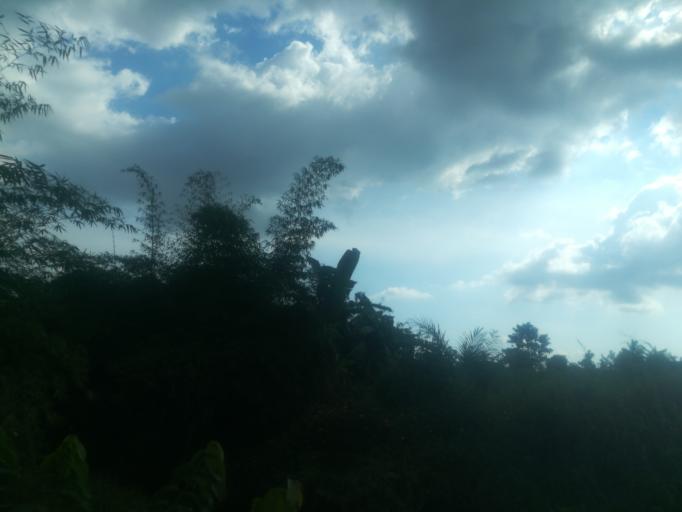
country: NG
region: Oyo
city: Ibadan
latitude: 7.4008
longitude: 3.8389
